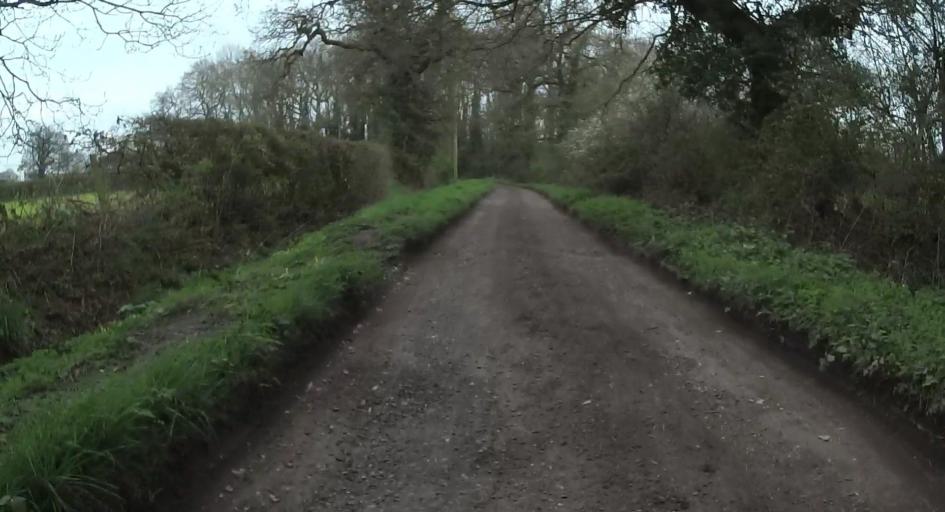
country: GB
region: England
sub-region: West Berkshire
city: Arborfield
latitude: 51.4056
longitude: -0.9101
